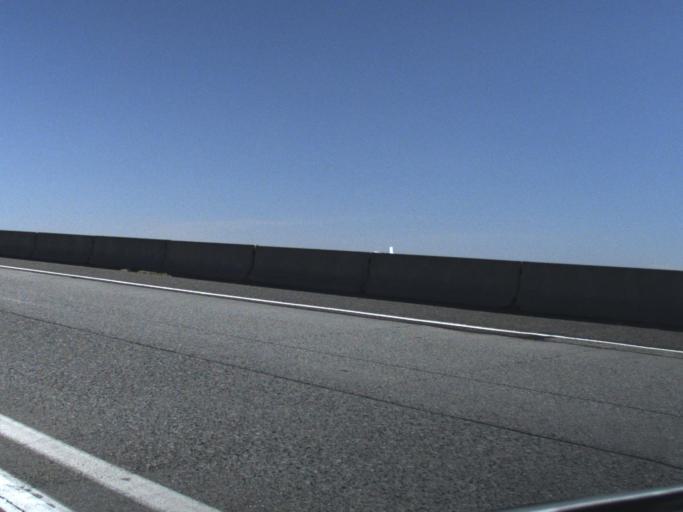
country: US
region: Washington
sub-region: Benton County
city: Richland
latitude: 46.2600
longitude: -119.2505
